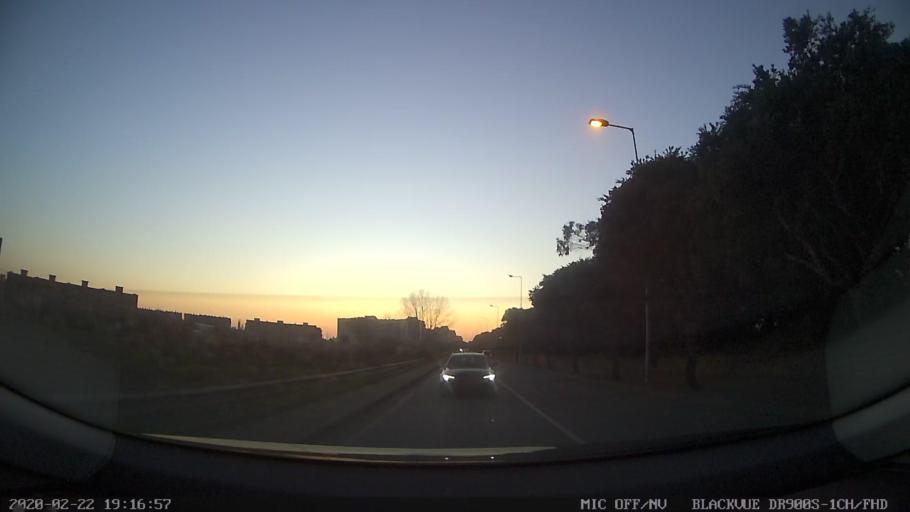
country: PT
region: Porto
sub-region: Matosinhos
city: Leca da Palmeira
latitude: 41.2014
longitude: -8.6997
